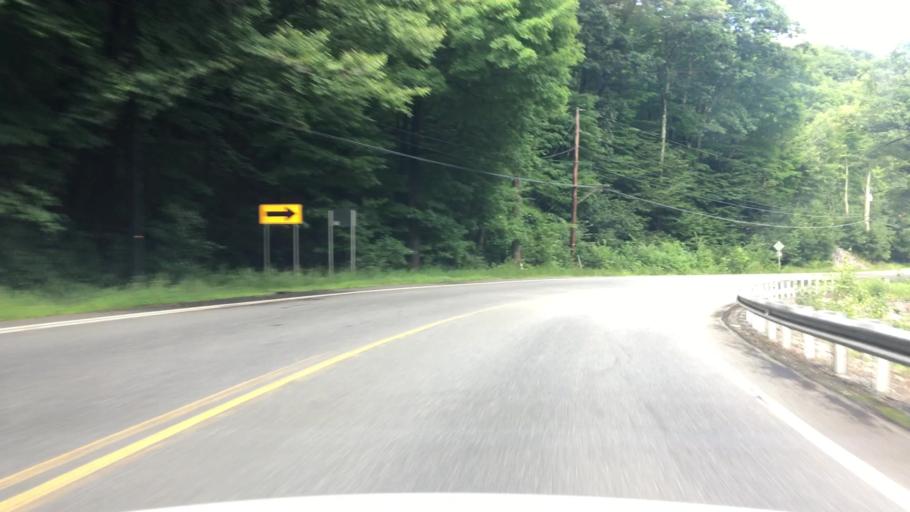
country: US
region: Vermont
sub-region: Windham County
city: West Brattleboro
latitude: 42.8776
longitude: -72.6842
